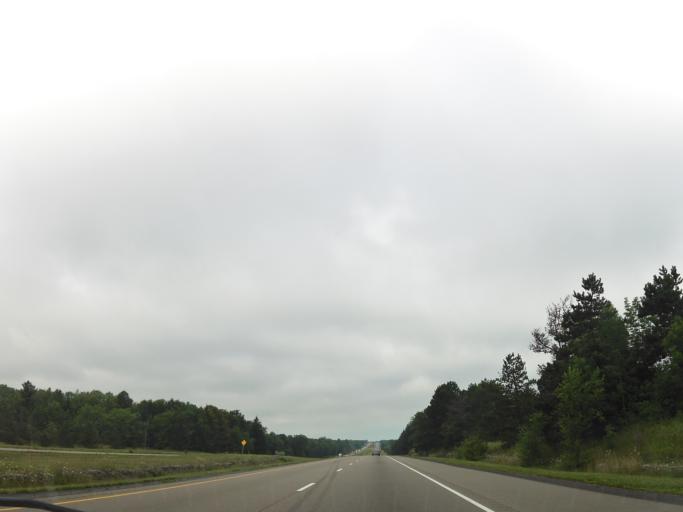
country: CA
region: Ontario
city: Skatepark
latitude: 44.2782
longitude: -76.8152
